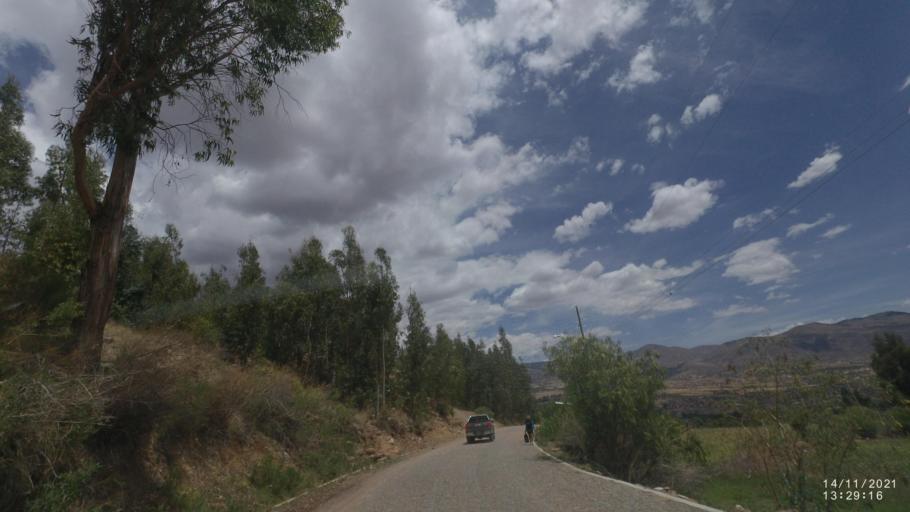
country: BO
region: Cochabamba
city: Colomi
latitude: -17.3885
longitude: -65.9840
